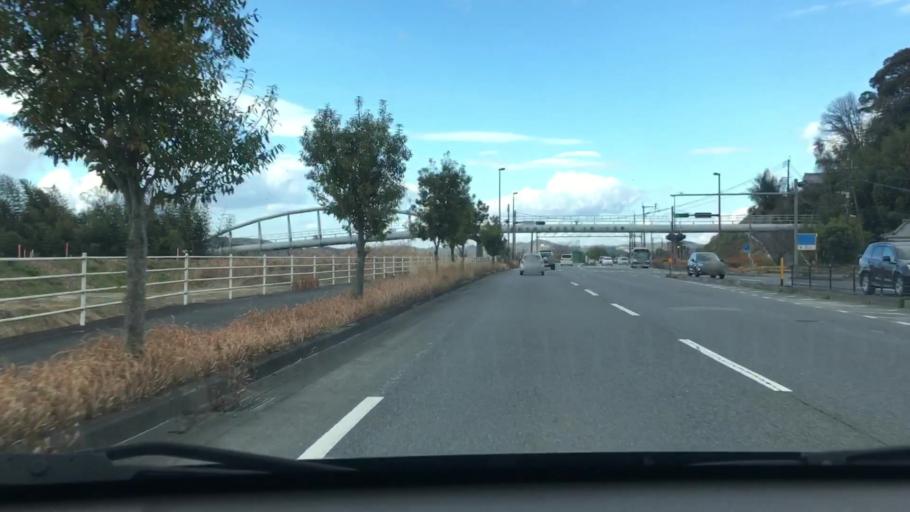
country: JP
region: Oita
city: Oita
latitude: 33.1358
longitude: 131.6597
